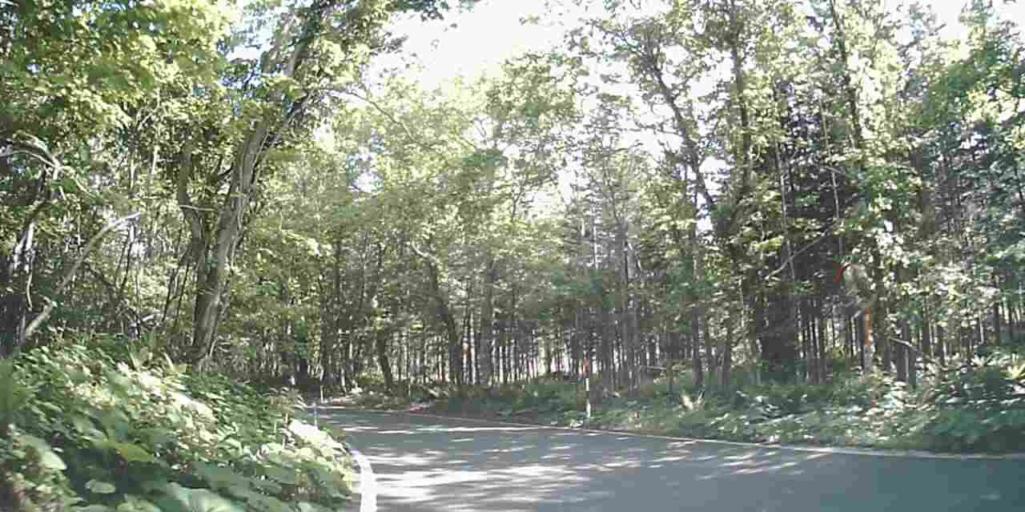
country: JP
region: Hokkaido
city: Shiraoi
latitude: 42.7288
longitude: 141.4135
